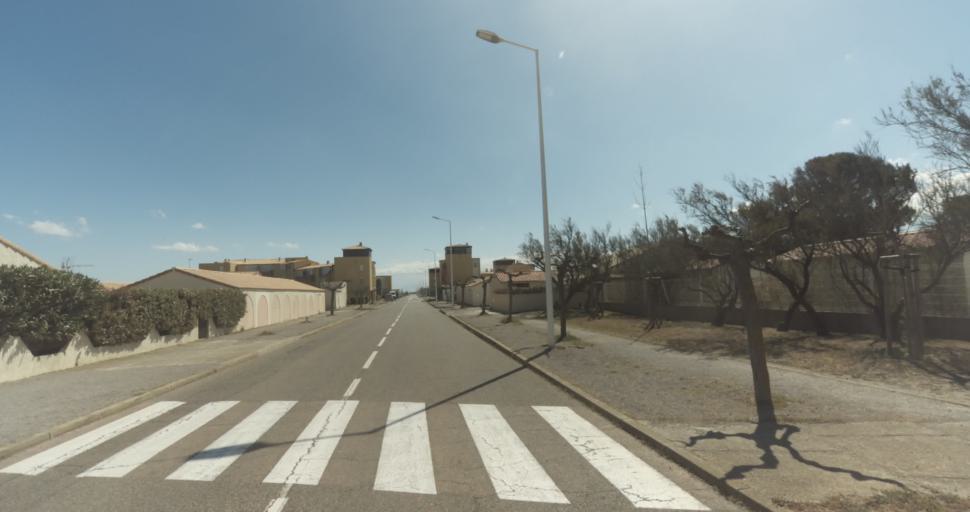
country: FR
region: Languedoc-Roussillon
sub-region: Departement des Pyrenees-Orientales
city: Le Barcares
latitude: 42.8478
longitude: 3.0422
